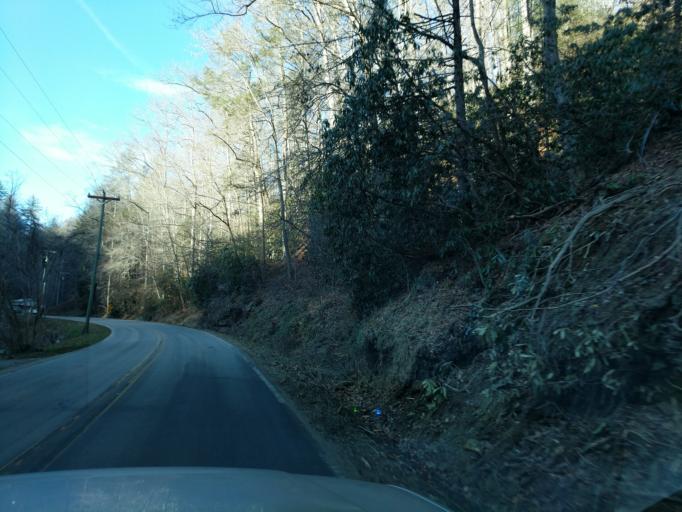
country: US
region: North Carolina
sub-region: Henderson County
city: Edneyville
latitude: 35.4529
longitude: -82.2970
